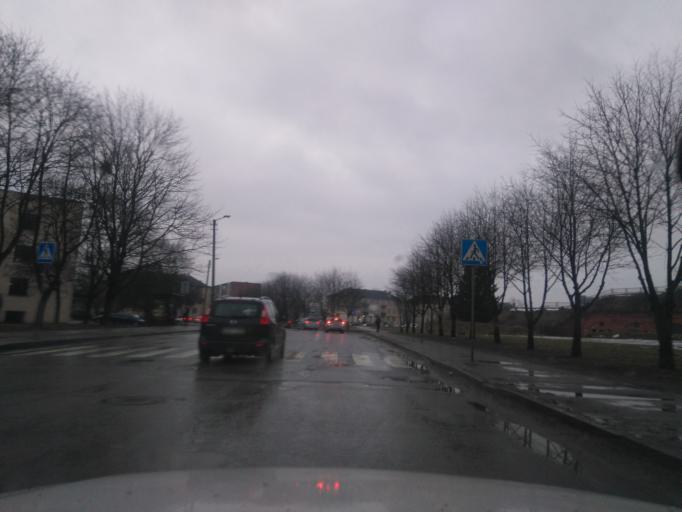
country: LT
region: Kauno apskritis
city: Dainava (Kaunas)
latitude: 54.8962
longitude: 23.9564
